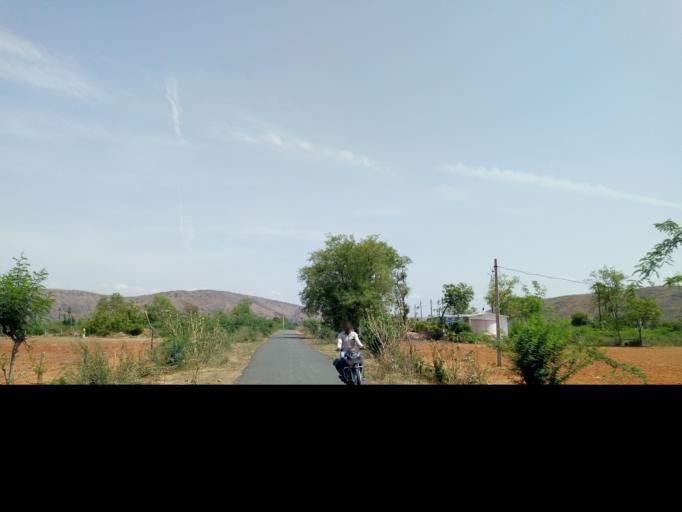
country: IN
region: Andhra Pradesh
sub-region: Prakasam
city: Cumbum
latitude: 15.7093
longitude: 79.0851
